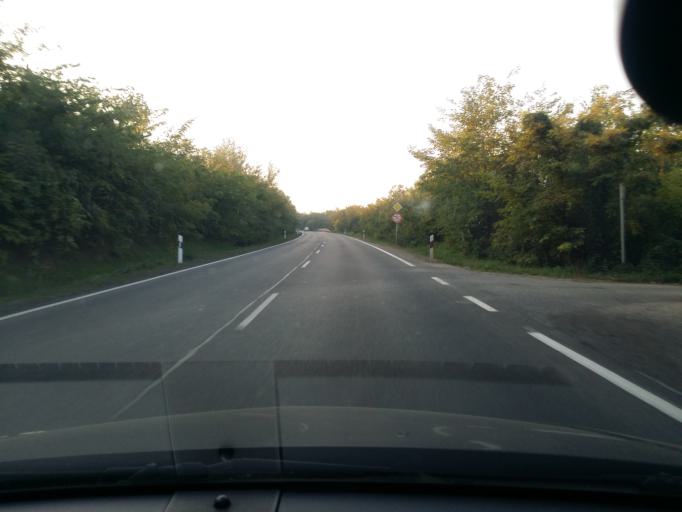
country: HU
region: Fejer
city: dunaujvaros
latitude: 46.9487
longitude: 18.9132
